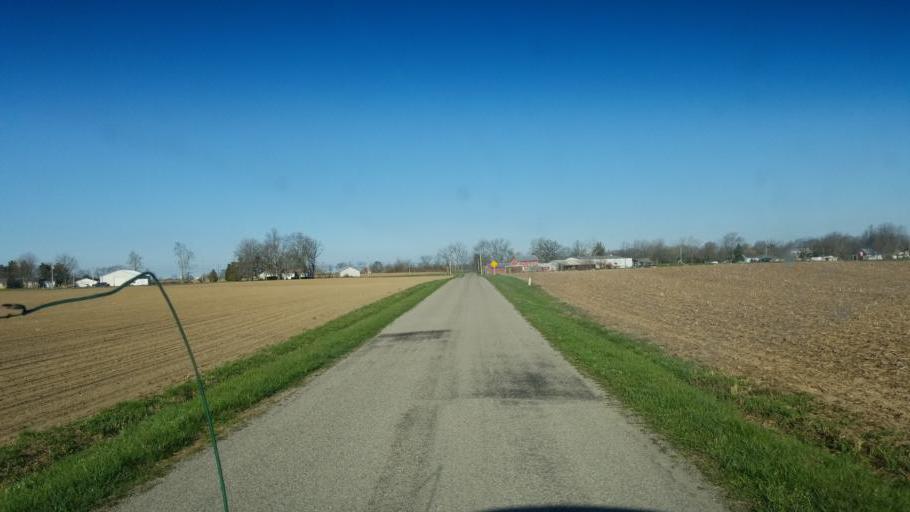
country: US
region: Ohio
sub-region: Union County
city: Richwood
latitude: 40.4506
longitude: -83.4483
